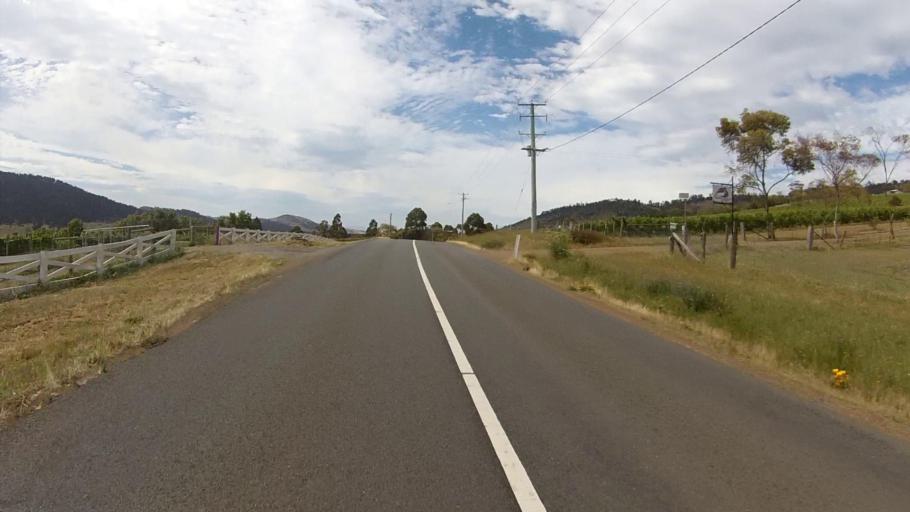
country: AU
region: Tasmania
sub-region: Brighton
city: Old Beach
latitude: -42.7075
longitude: 147.3690
